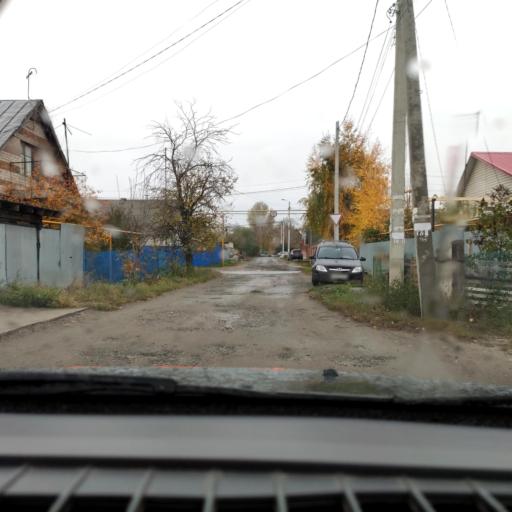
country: RU
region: Samara
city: Tol'yatti
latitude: 53.5350
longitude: 49.4253
